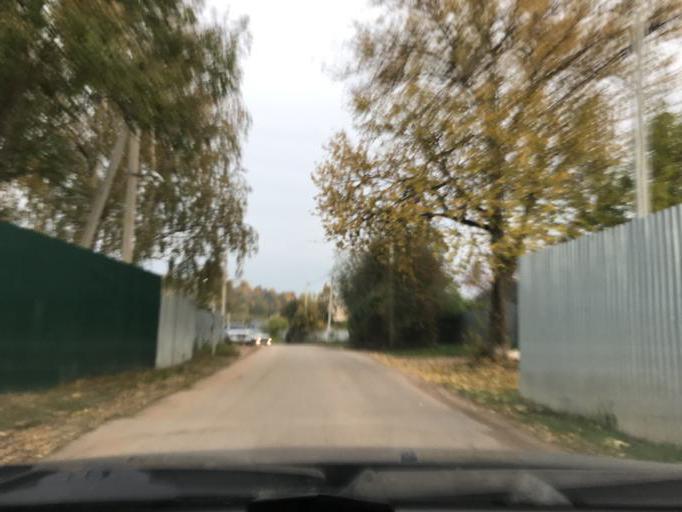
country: RU
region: Kaluga
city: Kaluga
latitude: 54.5500
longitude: 36.2238
